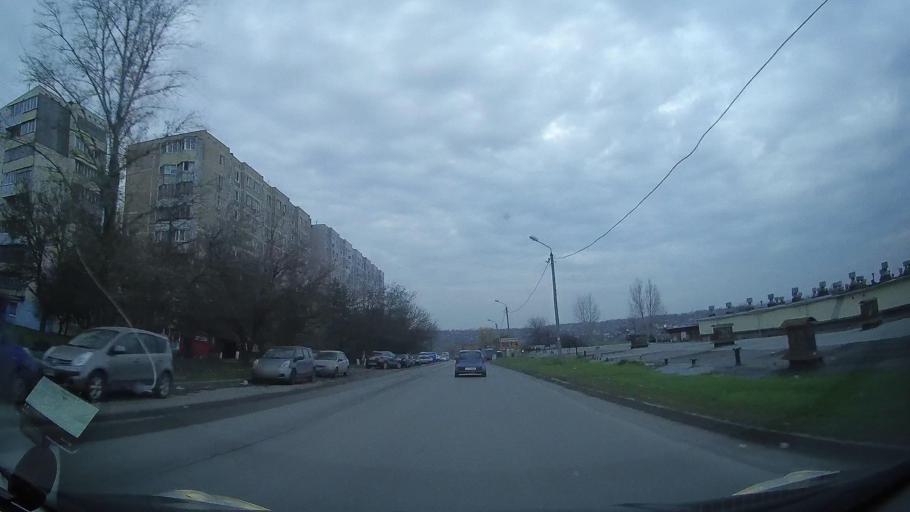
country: RU
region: Rostov
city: Severnyy
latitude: 47.2941
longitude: 39.6925
